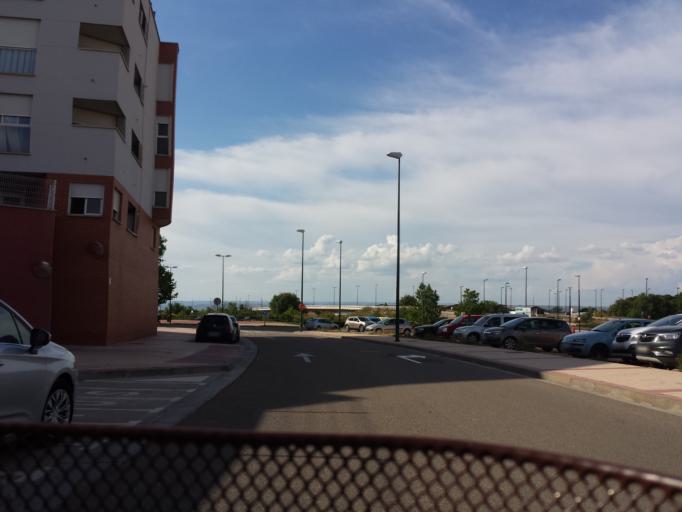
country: ES
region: Aragon
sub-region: Provincia de Zaragoza
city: Montecanal
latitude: 41.6383
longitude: -0.9446
